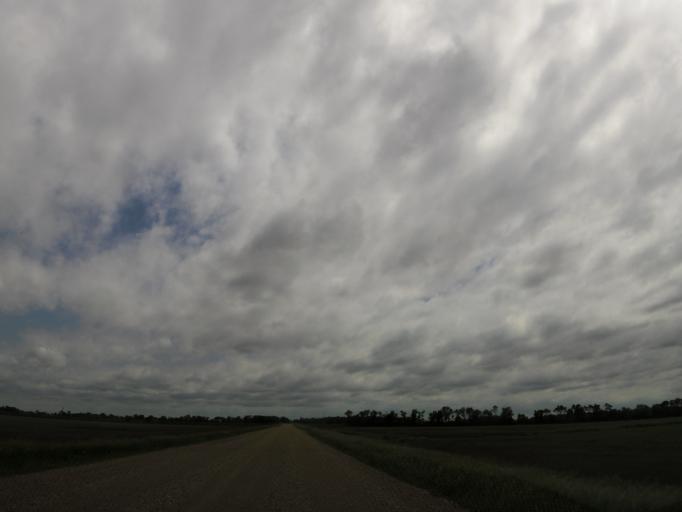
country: US
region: North Dakota
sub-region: Walsh County
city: Grafton
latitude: 48.4314
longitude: -97.4918
